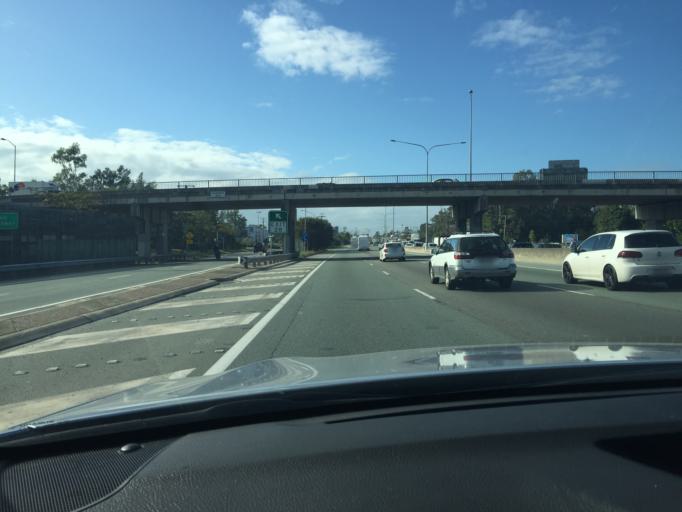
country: AU
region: Queensland
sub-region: Logan
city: Slacks Creek
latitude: -27.6560
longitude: 153.1652
